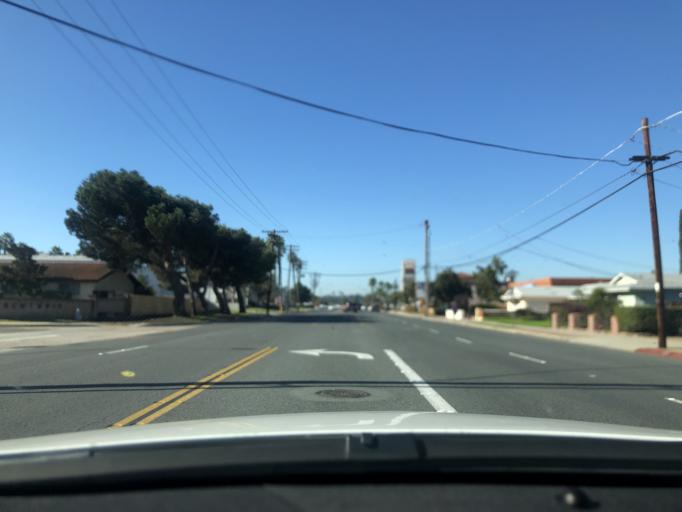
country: US
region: California
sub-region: San Diego County
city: El Cajon
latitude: 32.7804
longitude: -116.9550
